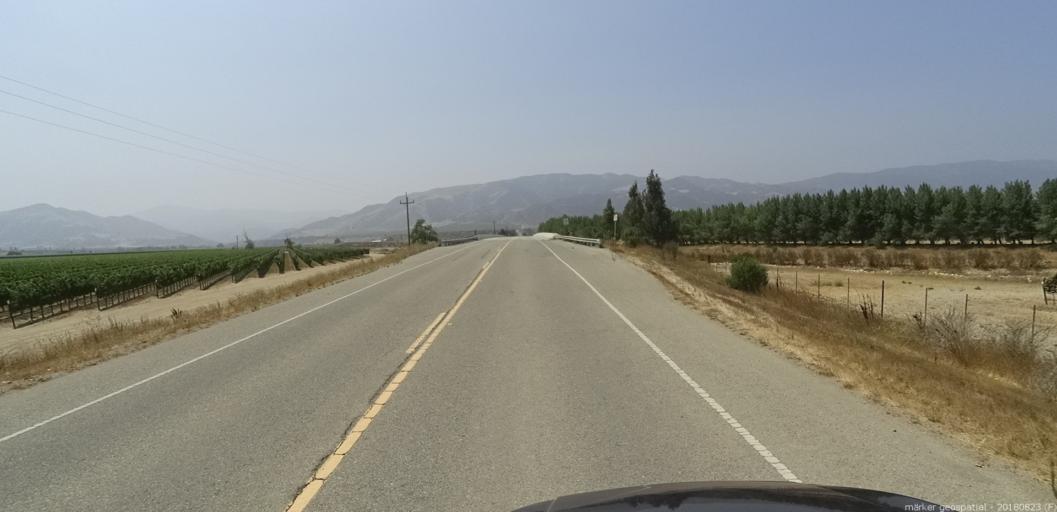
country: US
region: California
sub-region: Monterey County
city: Greenfield
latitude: 36.3237
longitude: -121.2911
